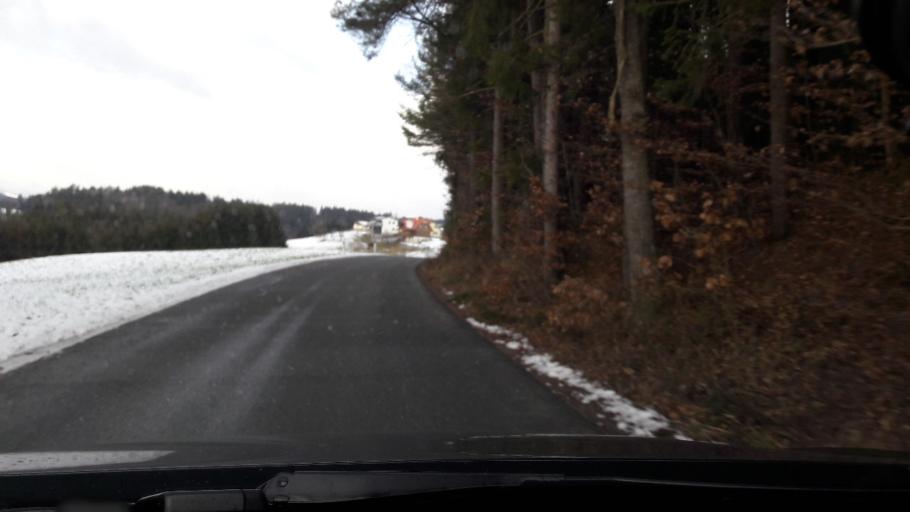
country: AT
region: Styria
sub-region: Politischer Bezirk Graz-Umgebung
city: Sankt Oswald bei Plankenwarth
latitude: 47.0925
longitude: 15.2560
